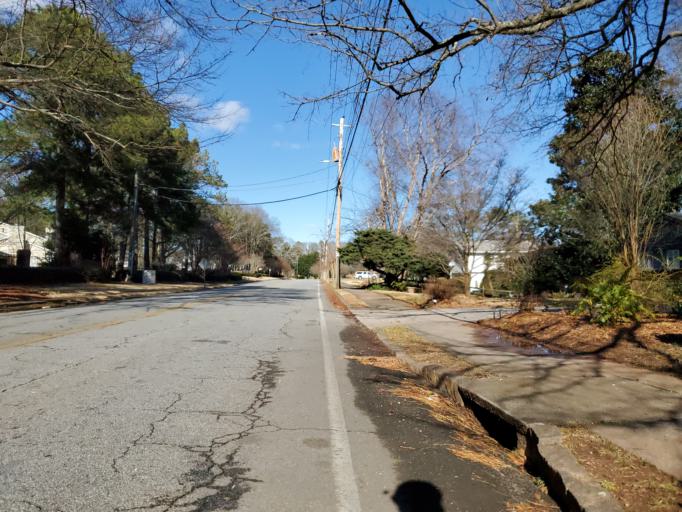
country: US
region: Georgia
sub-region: DeKalb County
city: Belvedere Park
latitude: 33.7617
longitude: -84.2677
